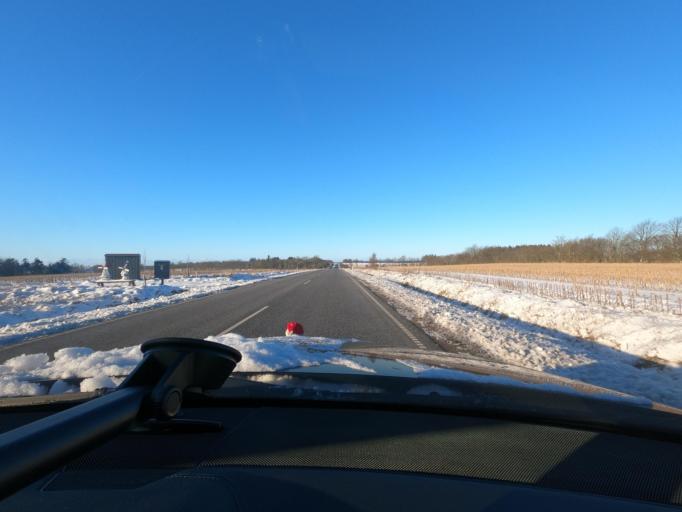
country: DK
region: South Denmark
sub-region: Tonder Kommune
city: Toftlund
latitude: 55.1146
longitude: 9.1668
